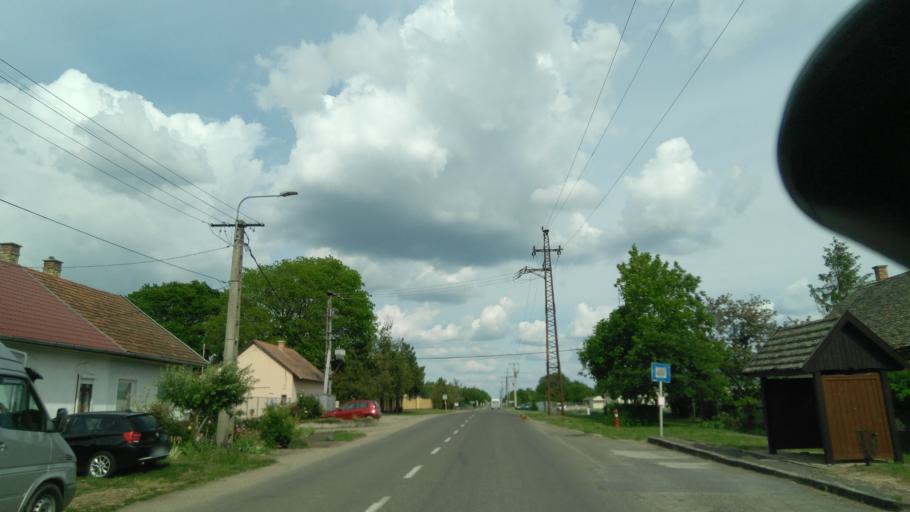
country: HU
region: Bekes
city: Mezohegyes
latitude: 46.3164
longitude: 20.8257
